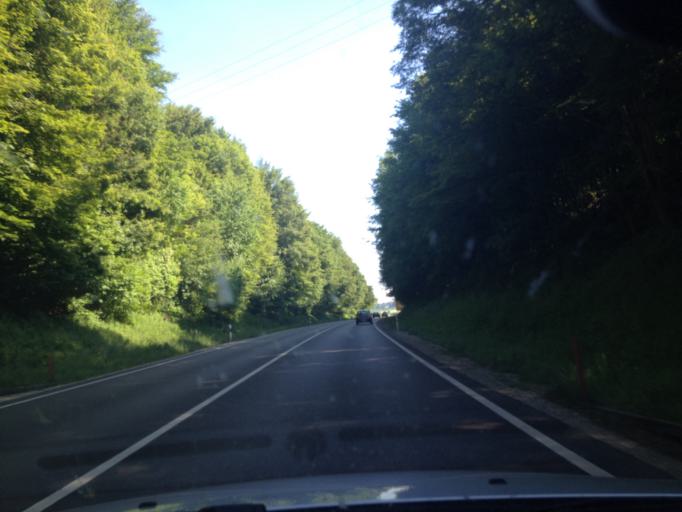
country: DE
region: Bavaria
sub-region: Swabia
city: Aichach
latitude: 48.4651
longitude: 11.1480
